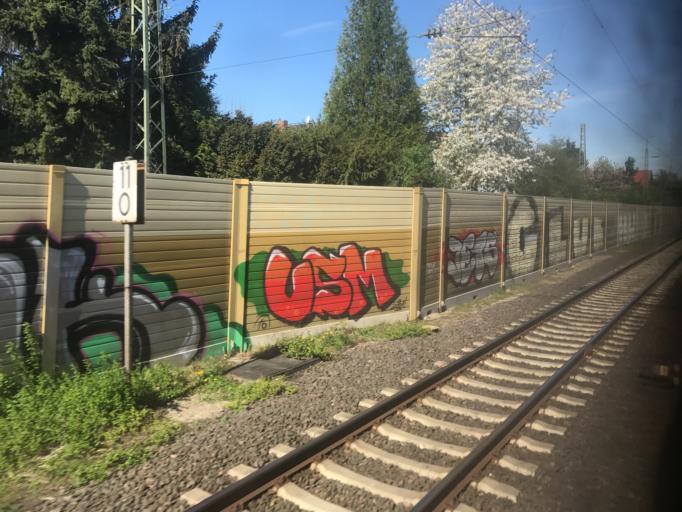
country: DE
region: Rheinland-Pfalz
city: Bodenheim
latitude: 49.9258
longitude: 8.3174
